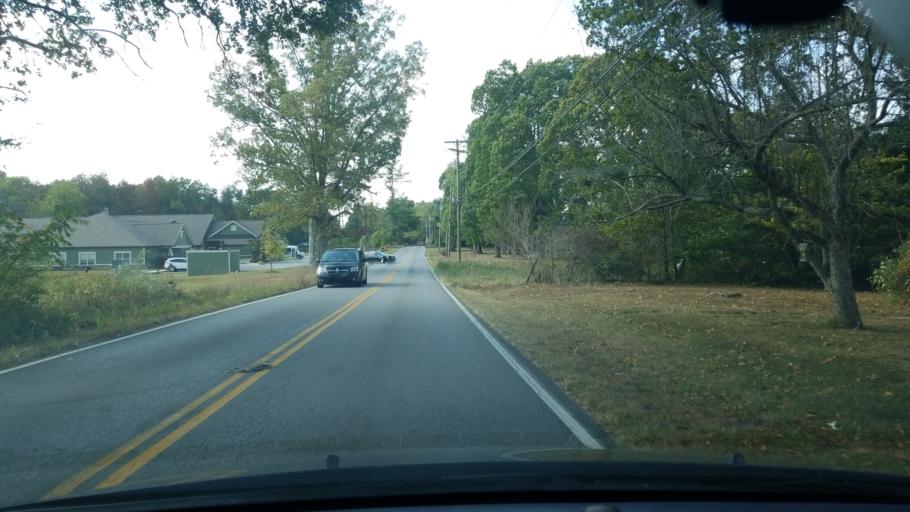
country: US
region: Tennessee
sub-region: Cumberland County
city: Crossville
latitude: 35.9802
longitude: -85.0280
